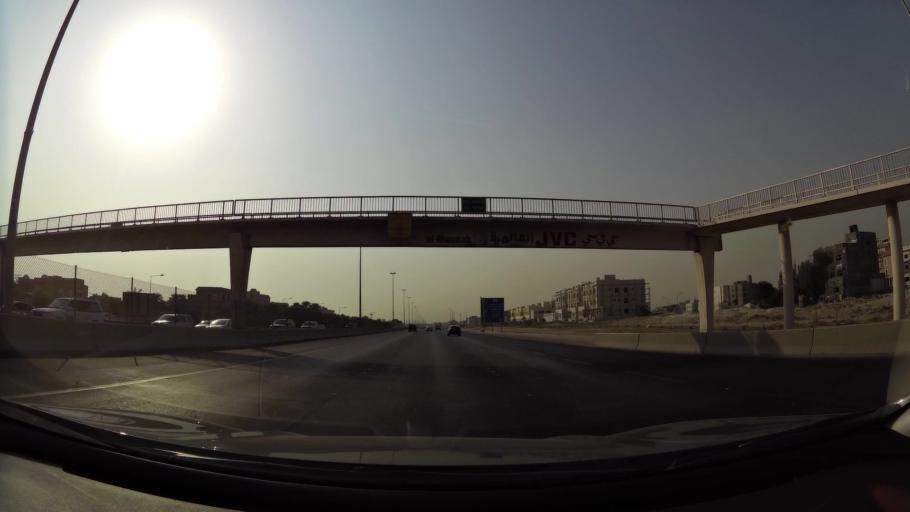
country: KW
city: Al Funaytis
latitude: 29.2266
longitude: 48.0988
